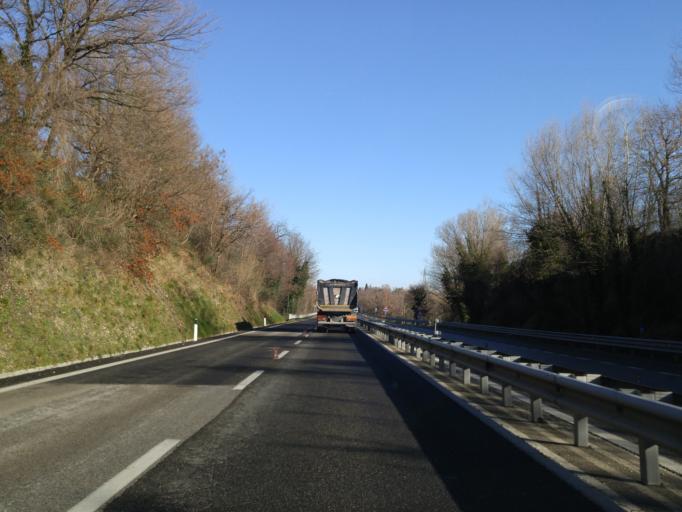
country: IT
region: The Marches
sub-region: Provincia di Pesaro e Urbino
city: Sant'Ippolito
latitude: 43.6937
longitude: 12.8600
